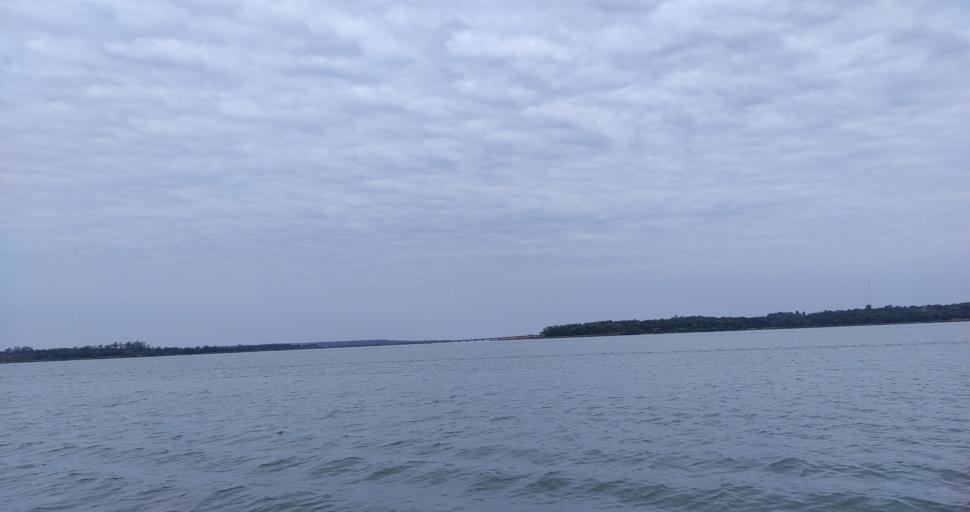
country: AR
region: Misiones
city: Garupa
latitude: -27.4416
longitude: -55.8104
